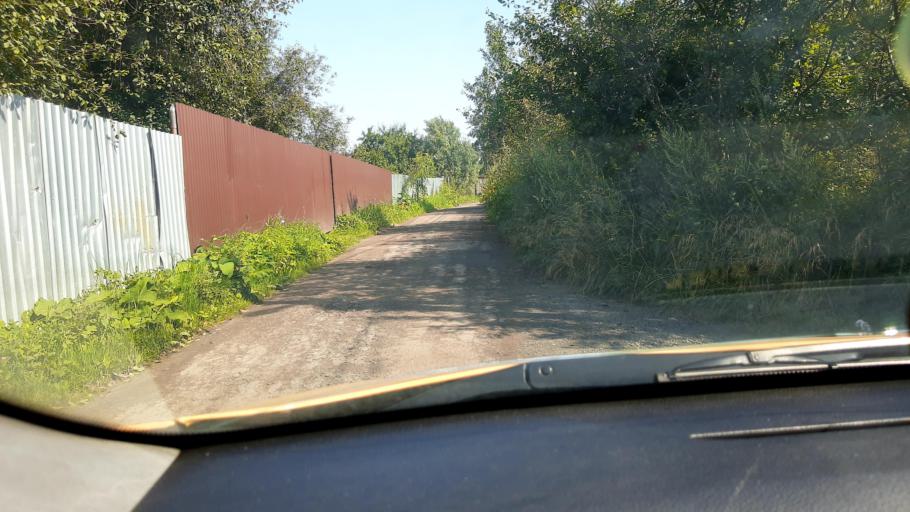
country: RU
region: Moscow
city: Zagor'ye
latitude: 55.5573
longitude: 37.6685
